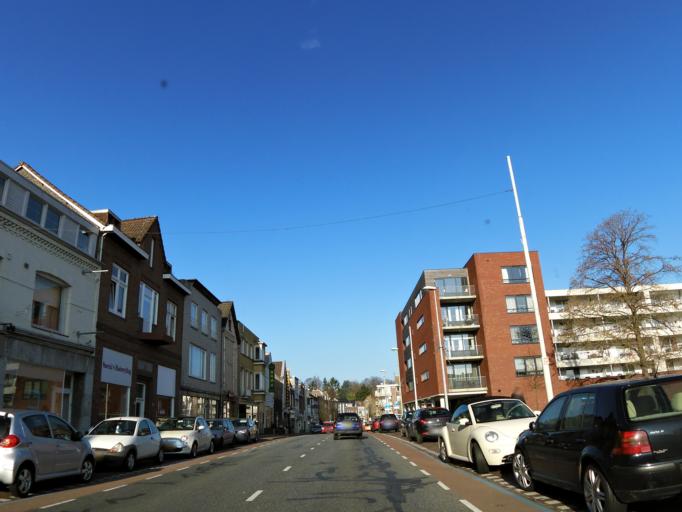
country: NL
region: Limburg
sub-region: Gemeente Brunssum
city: Brunssum
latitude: 50.9387
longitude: 5.9701
